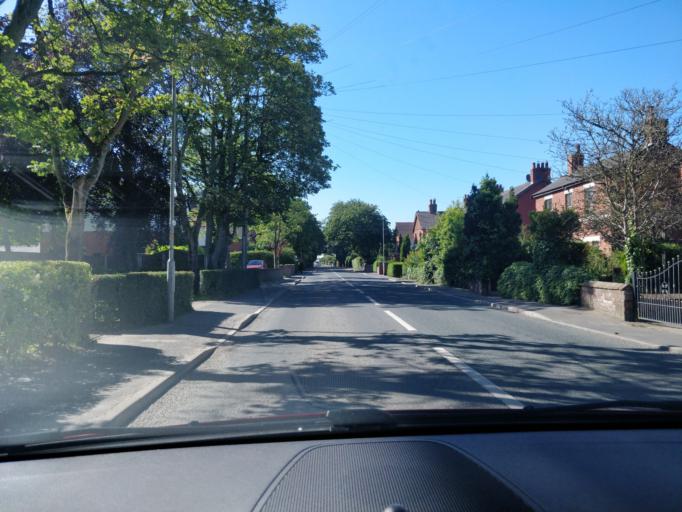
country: GB
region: England
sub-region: Lancashire
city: Tarleton
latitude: 53.6958
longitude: -2.8374
